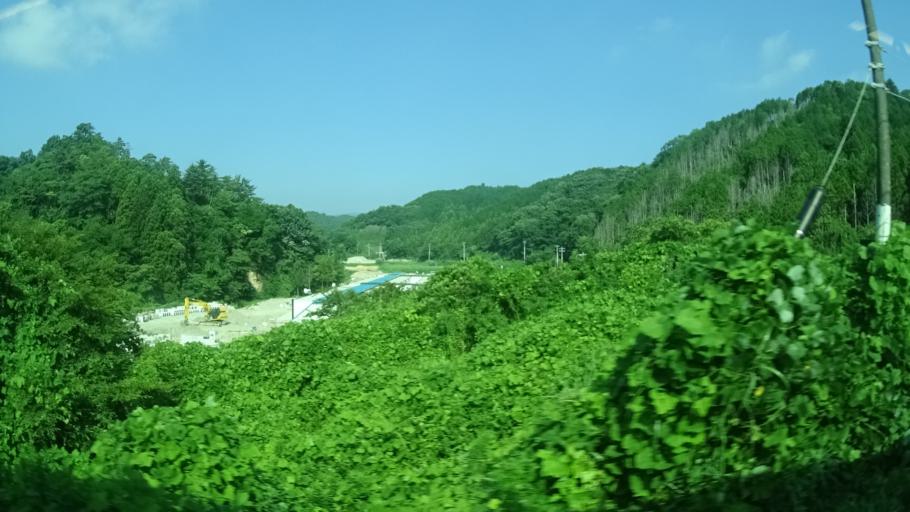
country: JP
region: Fukushima
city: Iwaki
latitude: 37.1846
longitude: 140.9992
